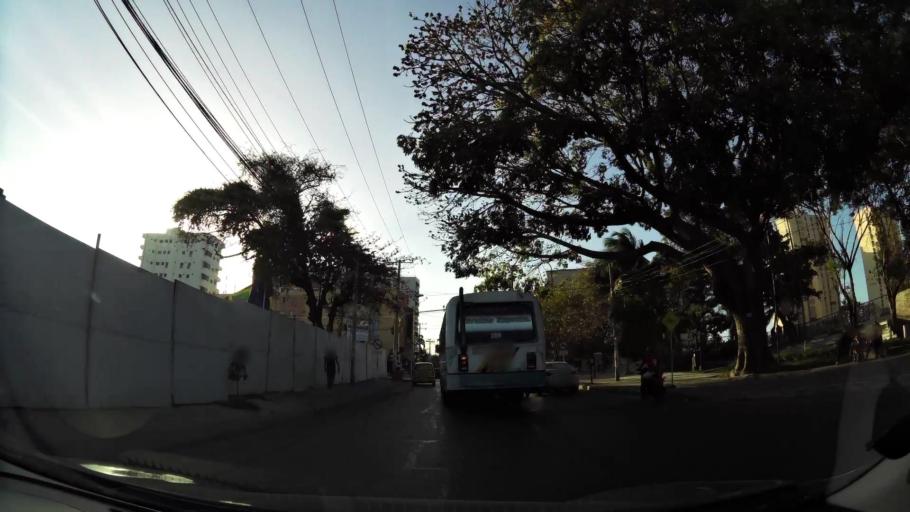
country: CO
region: Atlantico
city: Barranquilla
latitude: 10.9875
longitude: -74.7891
